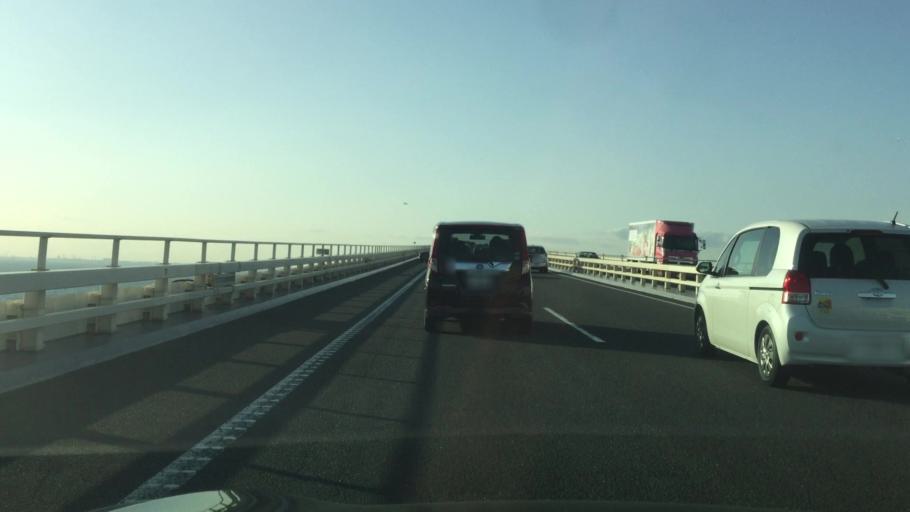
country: JP
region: Chiba
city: Kisarazu
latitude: 35.4511
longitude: 139.8937
